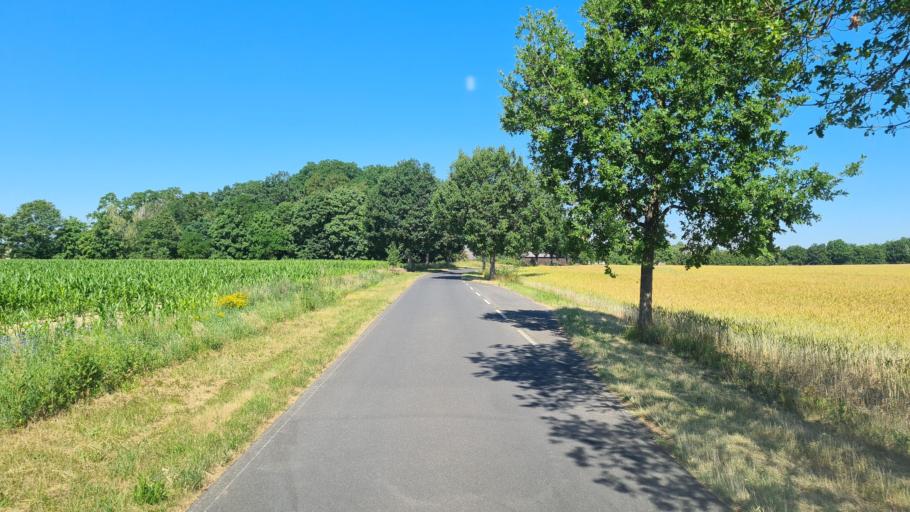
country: DE
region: Brandenburg
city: Niedergorsdorf
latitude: 52.0048
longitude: 12.9442
